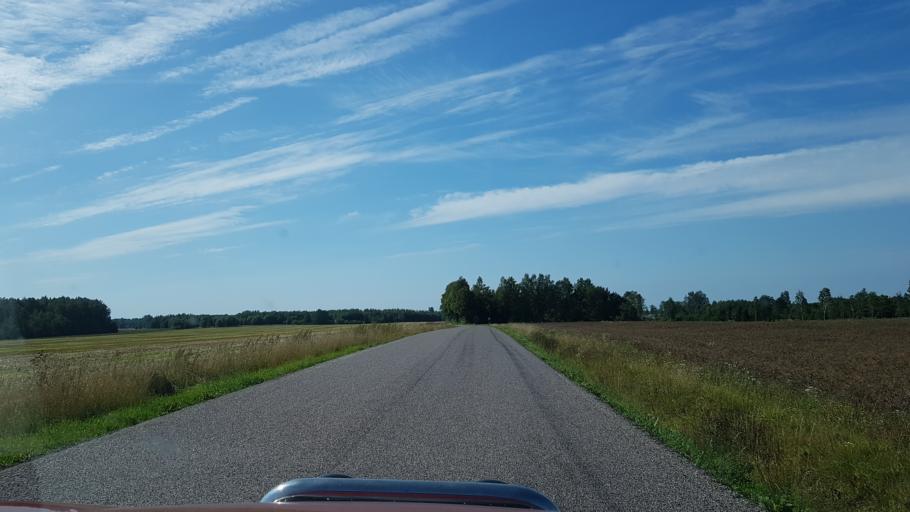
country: EE
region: Tartu
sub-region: Puhja vald
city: Puhja
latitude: 58.2559
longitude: 26.2880
